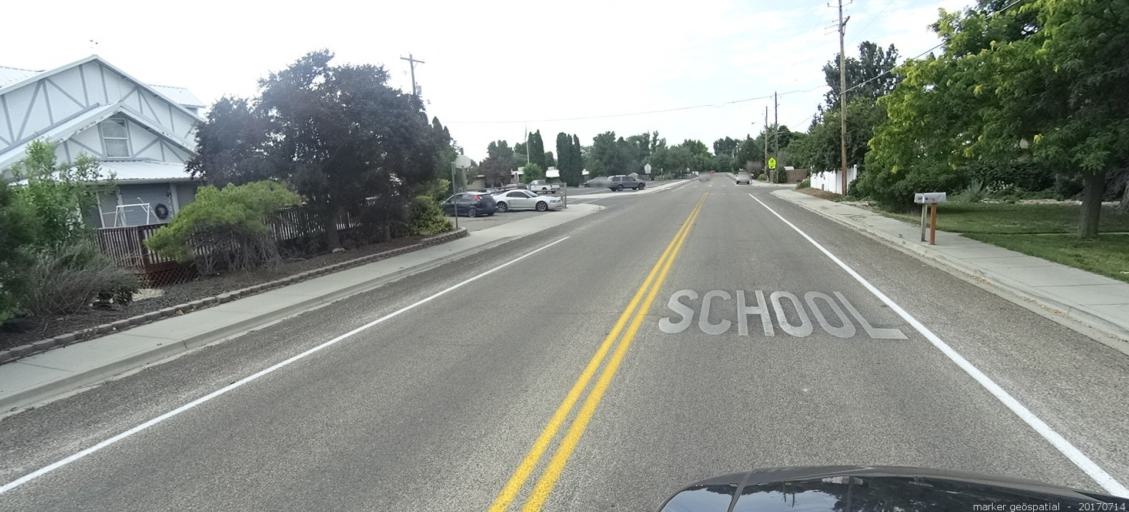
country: US
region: Idaho
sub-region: Ada County
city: Kuna
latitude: 43.4951
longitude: -116.4237
